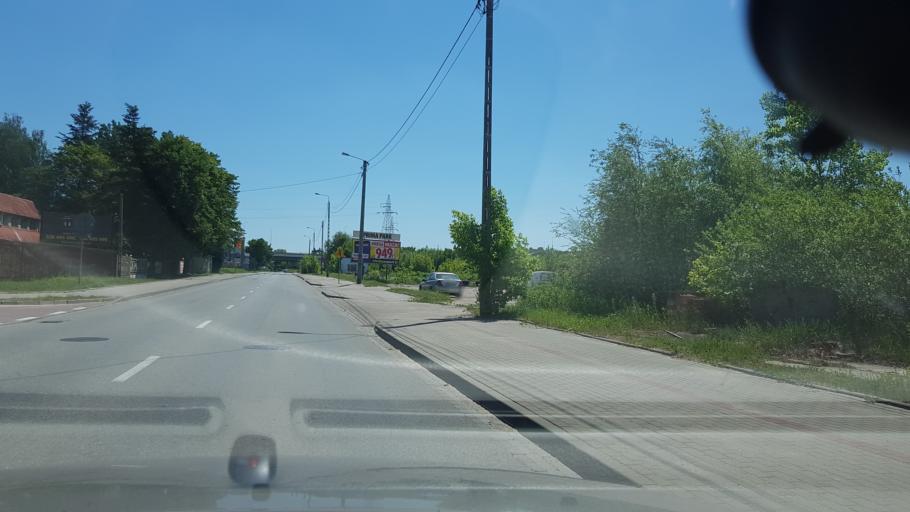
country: PL
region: Masovian Voivodeship
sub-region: Powiat wolominski
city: Marki
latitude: 52.3147
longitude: 21.1214
